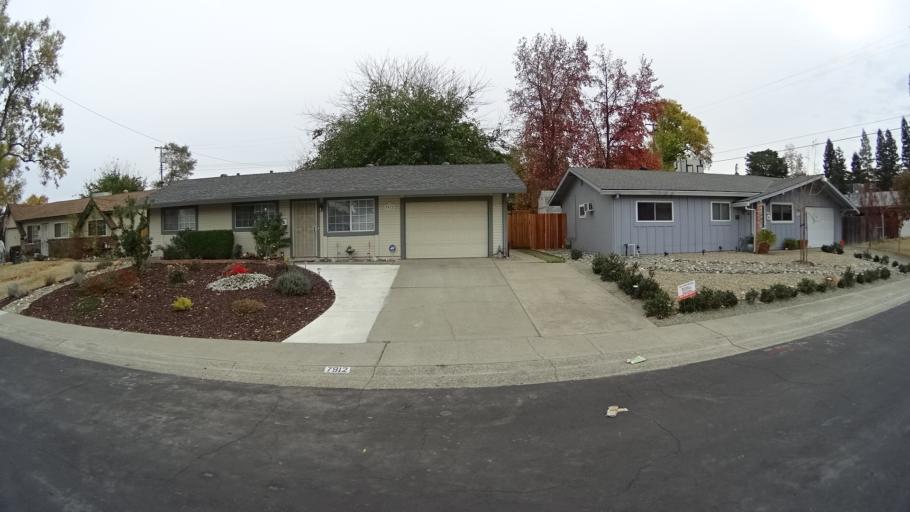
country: US
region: California
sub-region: Sacramento County
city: Citrus Heights
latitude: 38.7111
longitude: -121.2993
